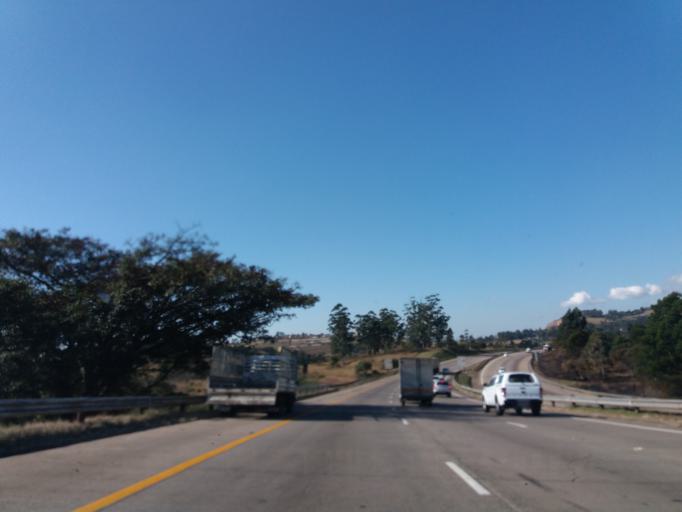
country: ZA
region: KwaZulu-Natal
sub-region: eThekwini Metropolitan Municipality
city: Mpumalanga
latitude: -29.7370
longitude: 30.6432
